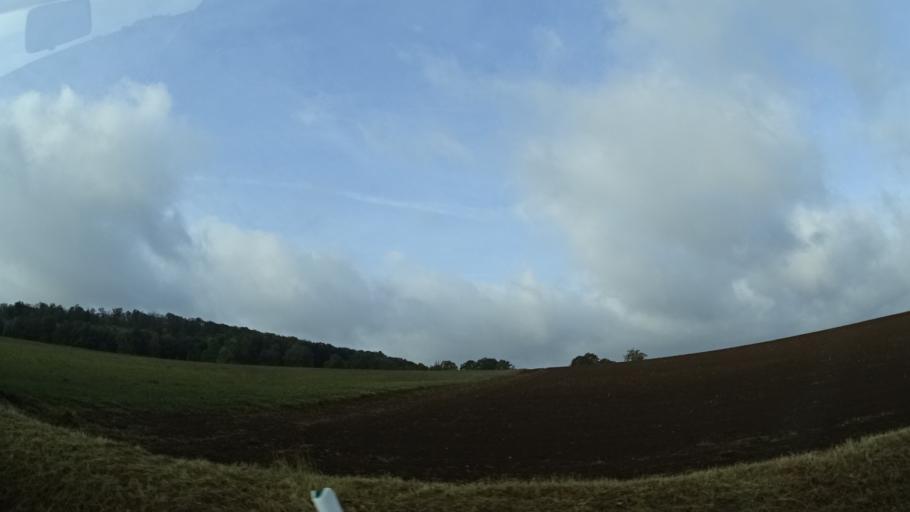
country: DE
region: Hesse
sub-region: Regierungsbezirk Giessen
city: Freiensteinau
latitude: 50.4720
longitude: 9.4062
